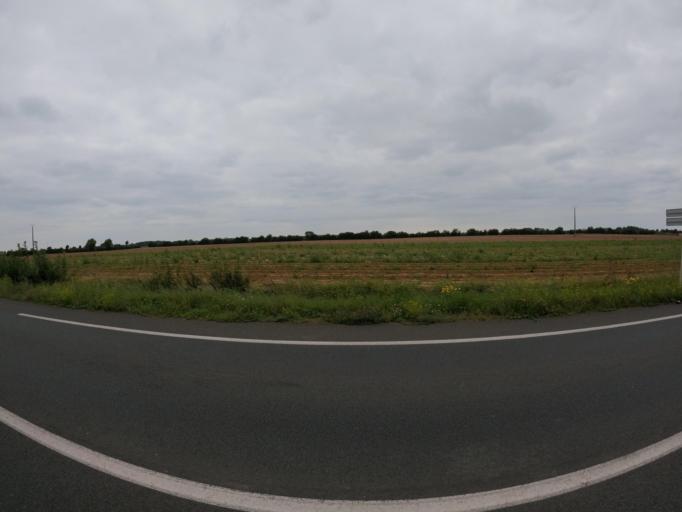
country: FR
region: Pays de la Loire
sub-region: Departement de la Vendee
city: Saint-Hilaire-des-Loges
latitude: 46.4071
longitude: -0.6803
